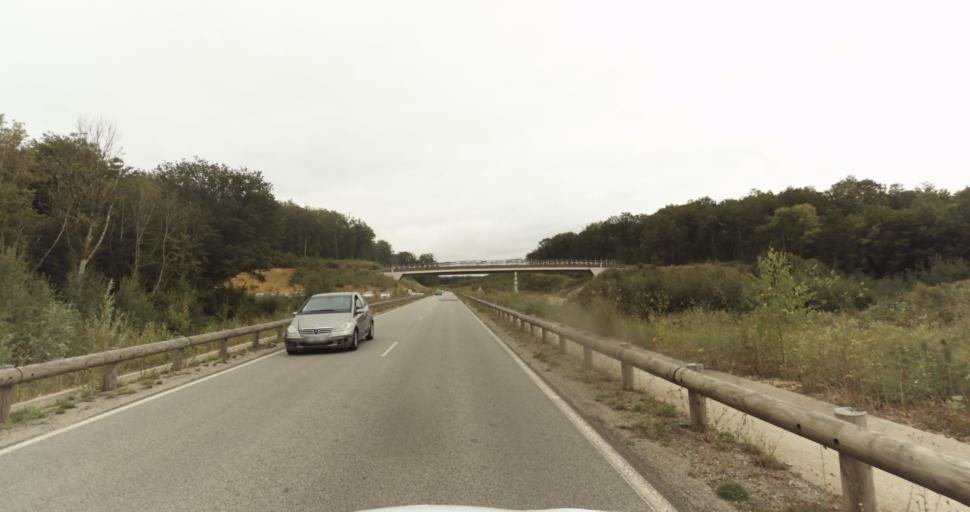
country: FR
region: Haute-Normandie
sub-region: Departement de l'Eure
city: Arnieres-sur-Iton
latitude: 49.0024
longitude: 1.1201
